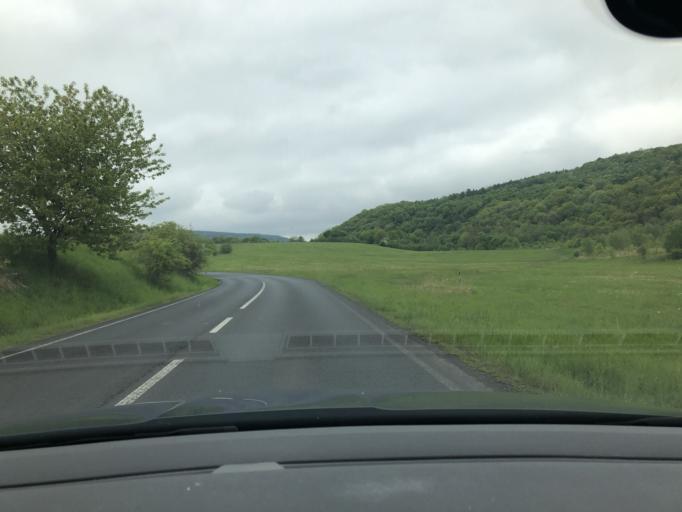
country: CZ
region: Ustecky
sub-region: Okres Usti nad Labem
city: Usti nad Labem
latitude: 50.7104
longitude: 14.0131
